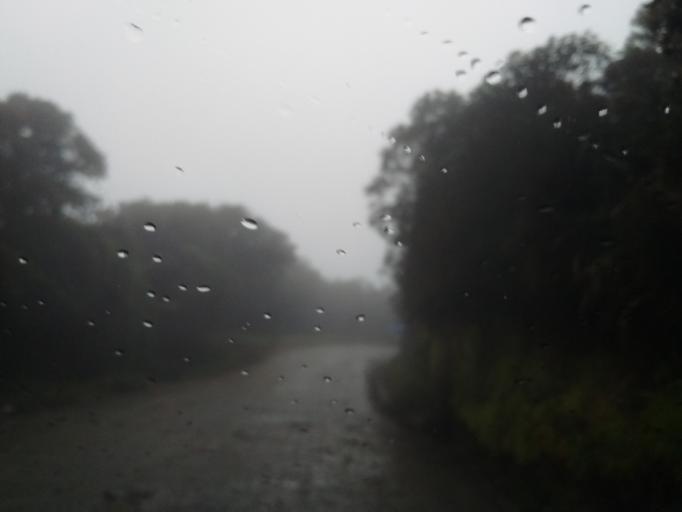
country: CO
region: Cauca
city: Paispamba
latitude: 2.1557
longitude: -76.4180
